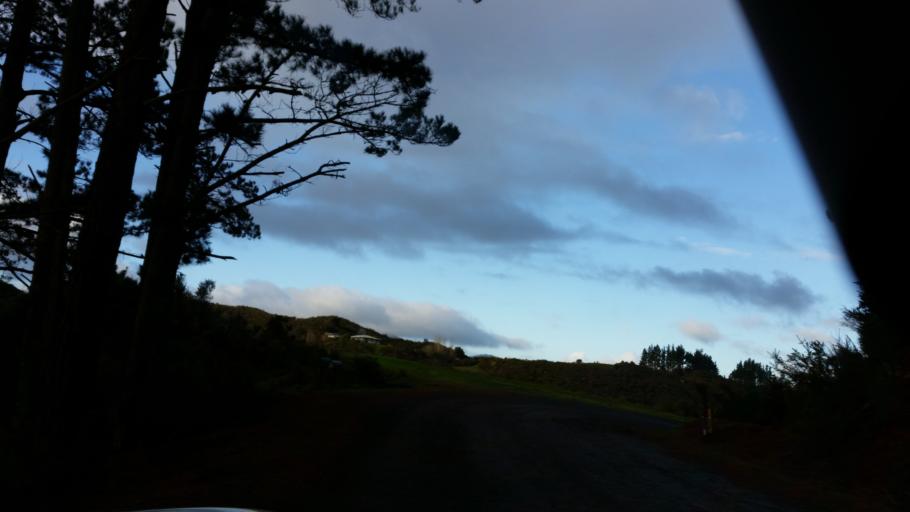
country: NZ
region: Northland
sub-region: Whangarei
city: Maungatapere
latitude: -35.7605
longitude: 174.0813
